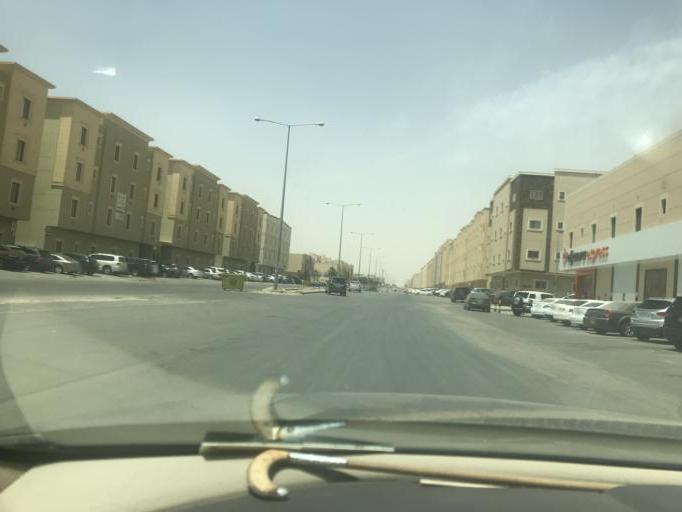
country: SA
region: Ar Riyad
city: Riyadh
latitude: 24.7989
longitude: 46.6634
